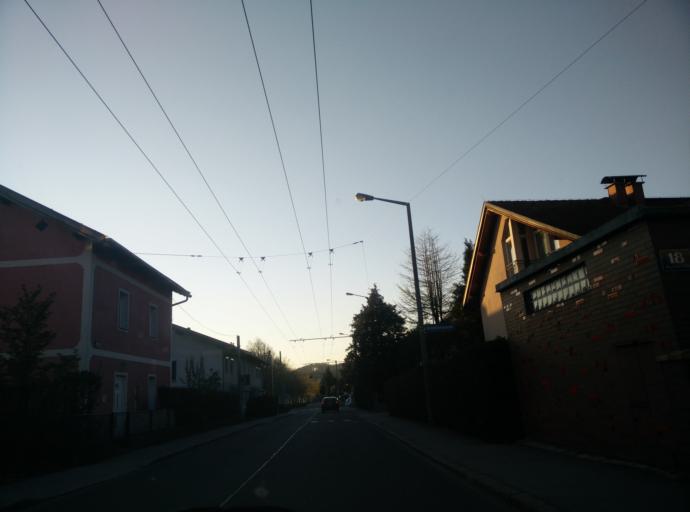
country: AT
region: Salzburg
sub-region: Salzburg Stadt
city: Salzburg
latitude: 47.8191
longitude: 13.0704
